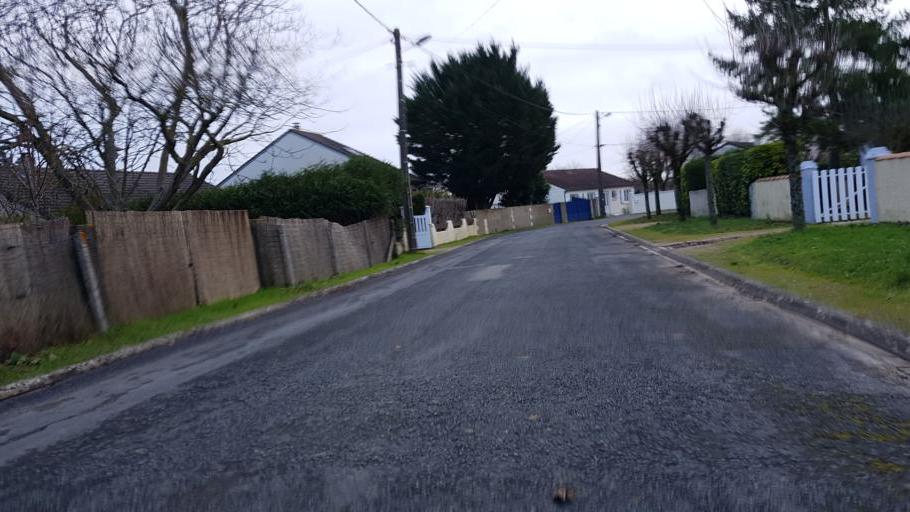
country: FR
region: Poitou-Charentes
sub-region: Departement de la Vienne
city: Avanton
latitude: 46.6655
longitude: 0.3112
